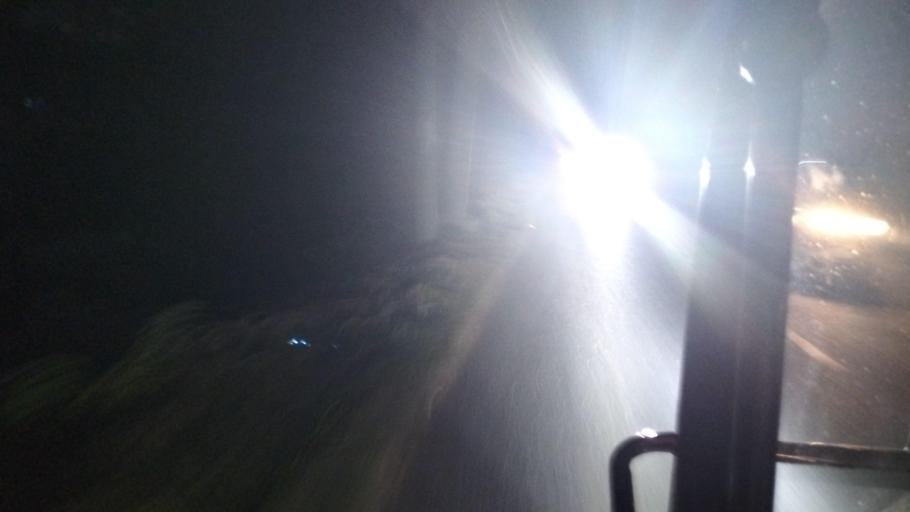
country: BD
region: Dhaka
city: Gafargaon
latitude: 24.4003
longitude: 90.3658
